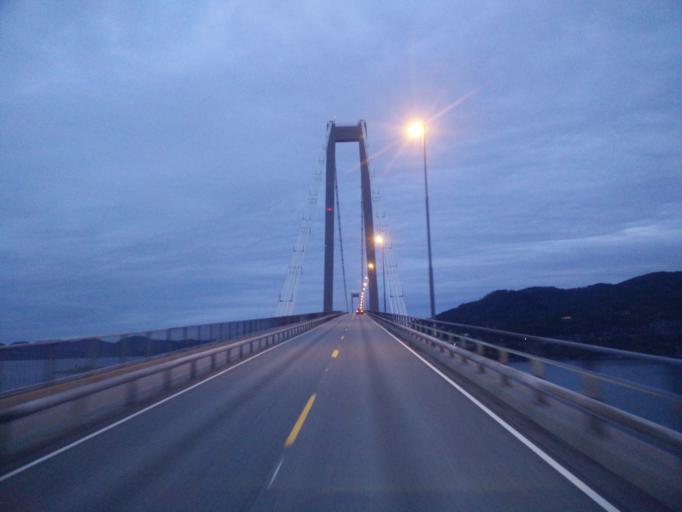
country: NO
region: More og Romsdal
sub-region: Gjemnes
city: Batnfjordsora
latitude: 62.9675
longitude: 7.7737
